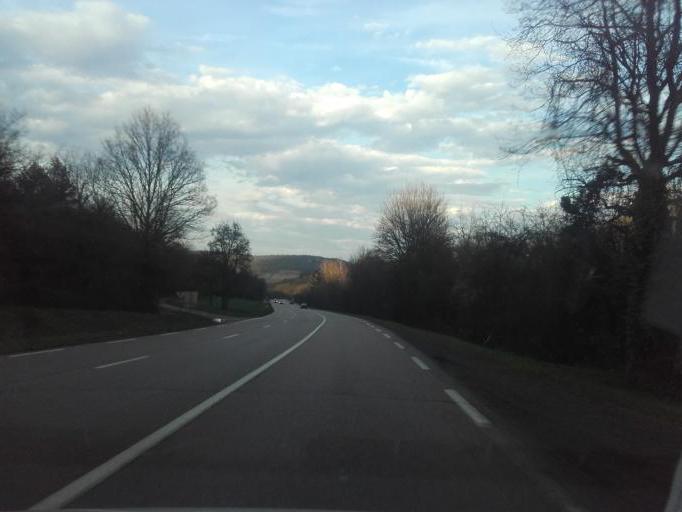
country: FR
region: Bourgogne
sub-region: Departement de la Cote-d'Or
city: Corpeau
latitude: 46.9416
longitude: 4.6992
